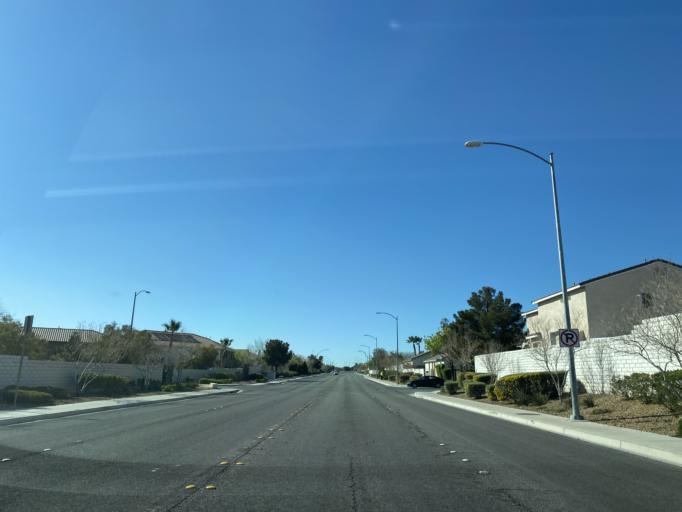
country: US
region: Nevada
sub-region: Clark County
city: Summerlin South
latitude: 36.3127
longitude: -115.2877
